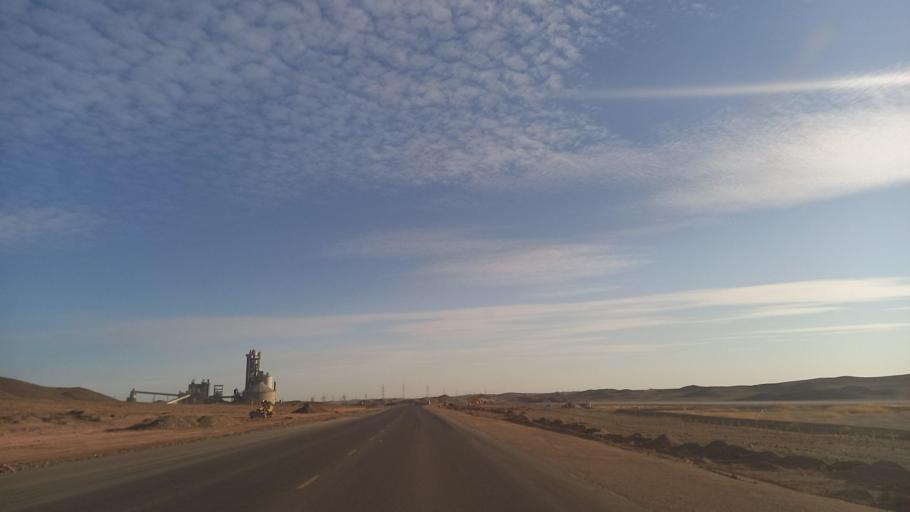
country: KZ
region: Zhambyl
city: Mynaral
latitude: 45.3968
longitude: 73.6412
